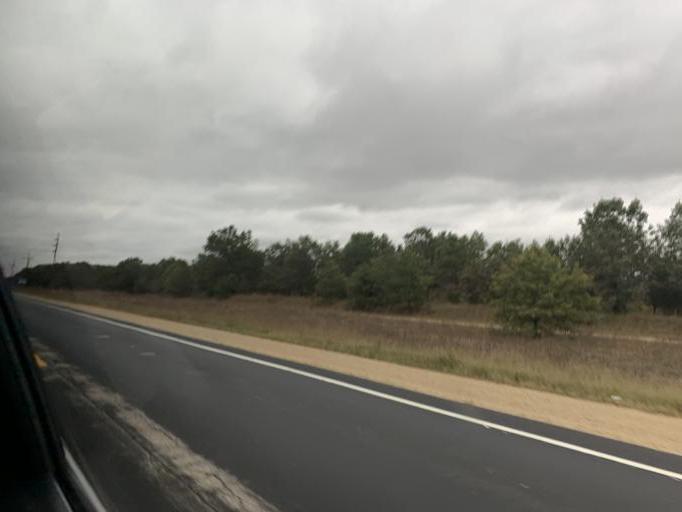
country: US
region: Wisconsin
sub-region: Sauk County
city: Spring Green
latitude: 43.1964
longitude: -90.2339
